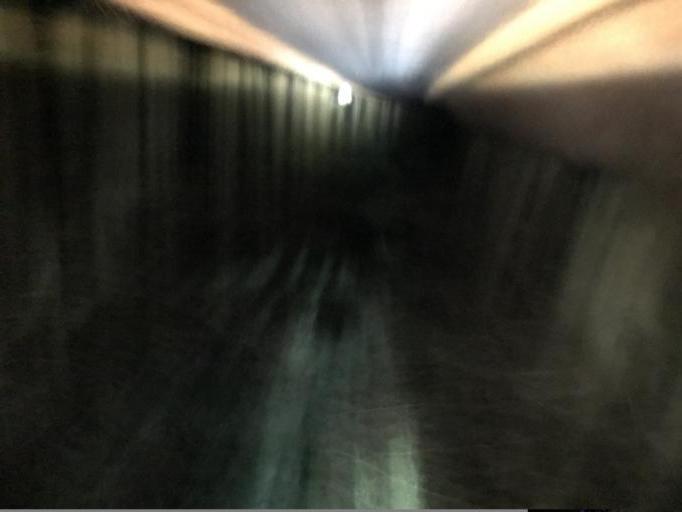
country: FR
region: Auvergne
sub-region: Departement du Puy-de-Dome
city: Saint-Remy-sur-Durolle
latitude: 45.9436
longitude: 3.6324
